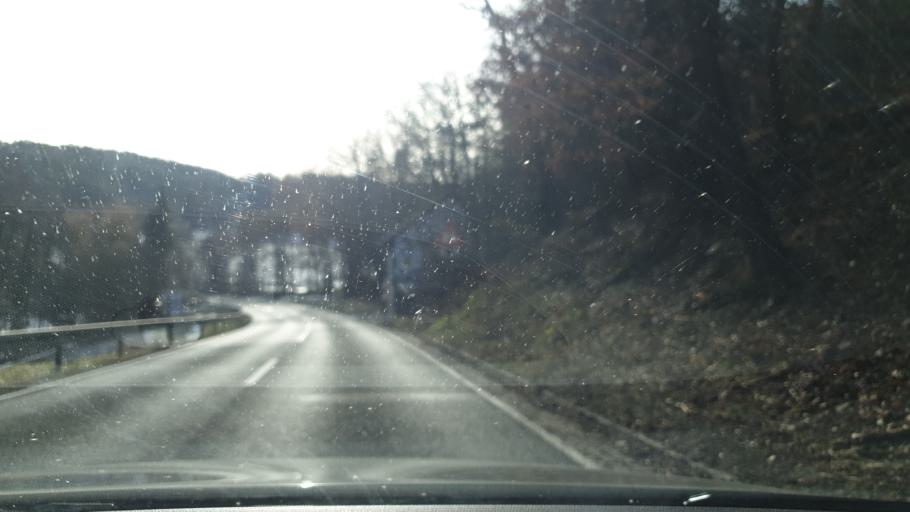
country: DE
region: Thuringia
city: Hohenolsen
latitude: 50.7268
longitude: 12.0688
